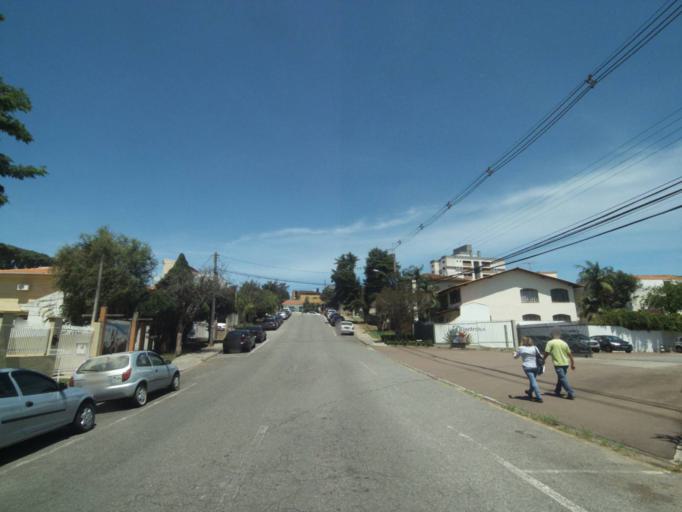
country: BR
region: Parana
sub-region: Pinhais
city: Pinhais
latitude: -25.4682
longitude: -49.2391
